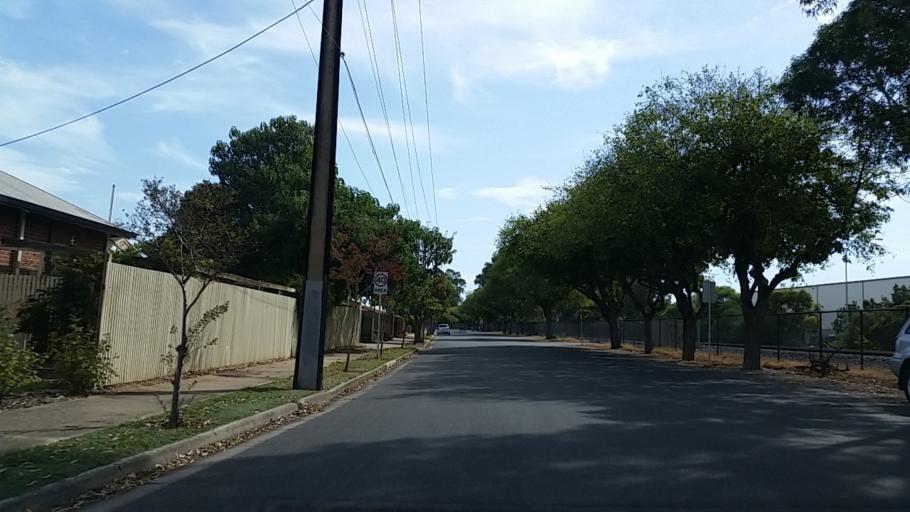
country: AU
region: South Australia
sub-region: Charles Sturt
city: Woodville North
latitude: -34.8761
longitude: 138.5339
